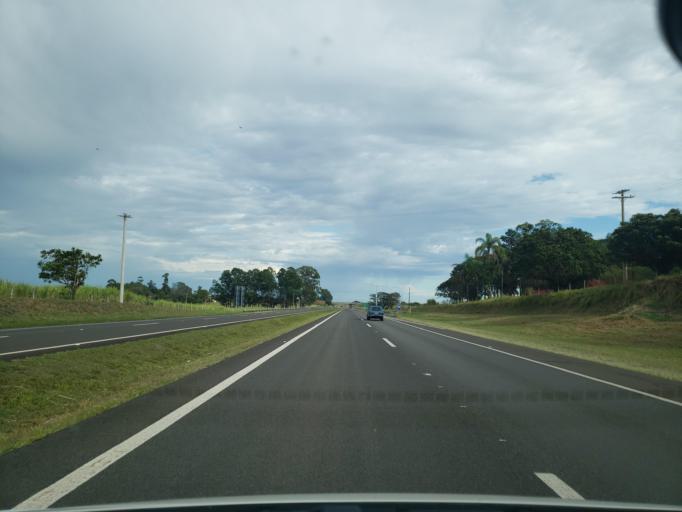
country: BR
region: Sao Paulo
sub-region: Dois Corregos
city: Dois Corregos
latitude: -22.2655
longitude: -48.4341
